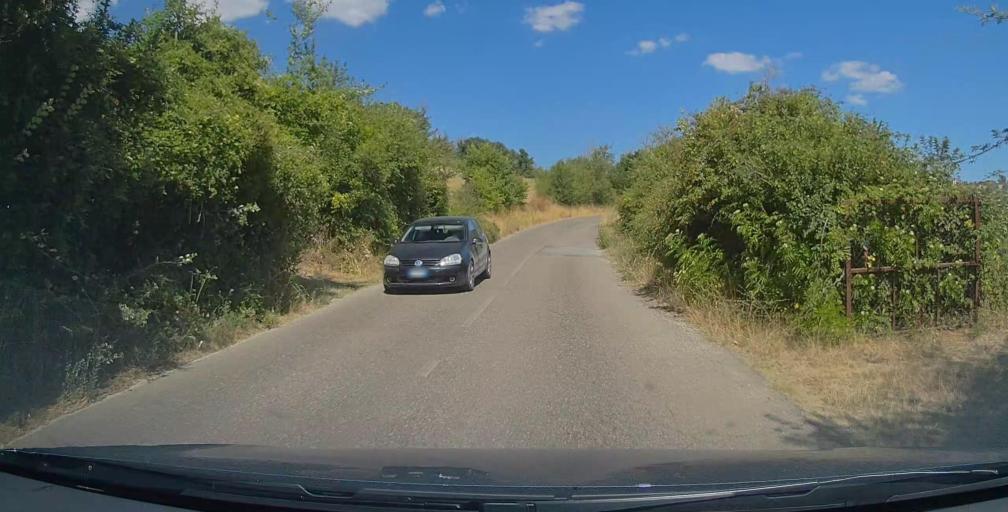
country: IT
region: Umbria
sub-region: Provincia di Terni
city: Otricoli
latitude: 42.3981
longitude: 12.4744
